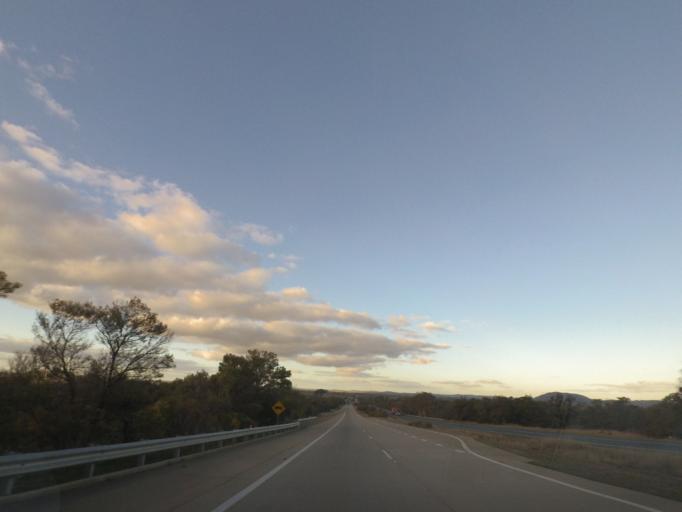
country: AU
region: New South Wales
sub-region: Yass Valley
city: Yass
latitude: -34.7750
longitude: 148.7344
